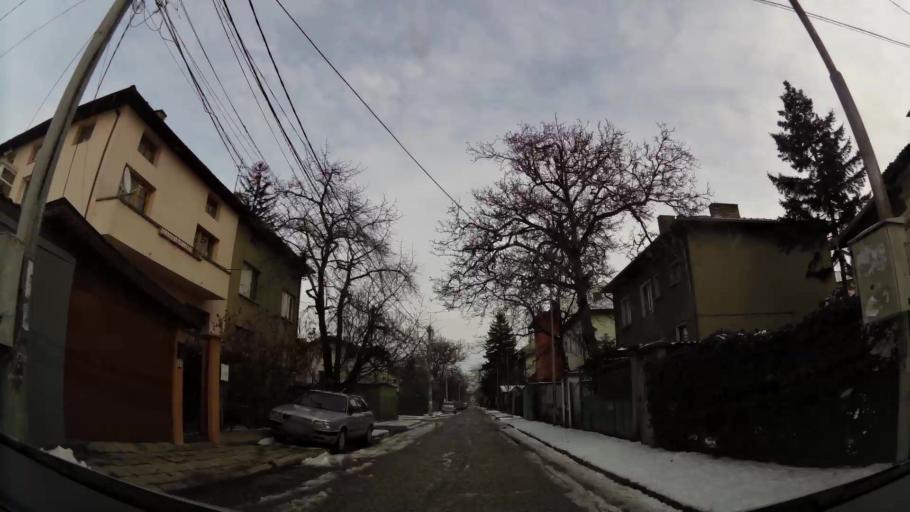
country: BG
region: Sofia-Capital
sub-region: Stolichna Obshtina
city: Sofia
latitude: 42.6974
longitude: 23.3681
